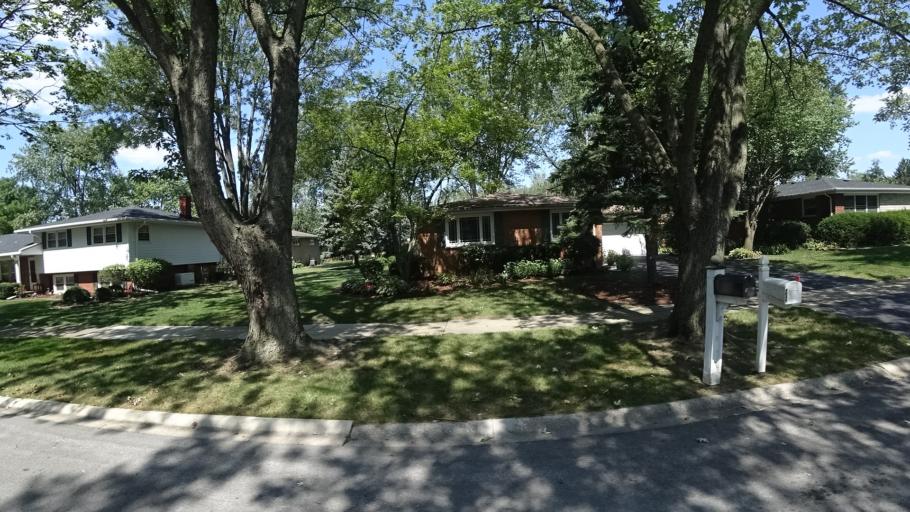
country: US
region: Illinois
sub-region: Cook County
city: Orland Park
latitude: 41.6295
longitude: -87.8310
